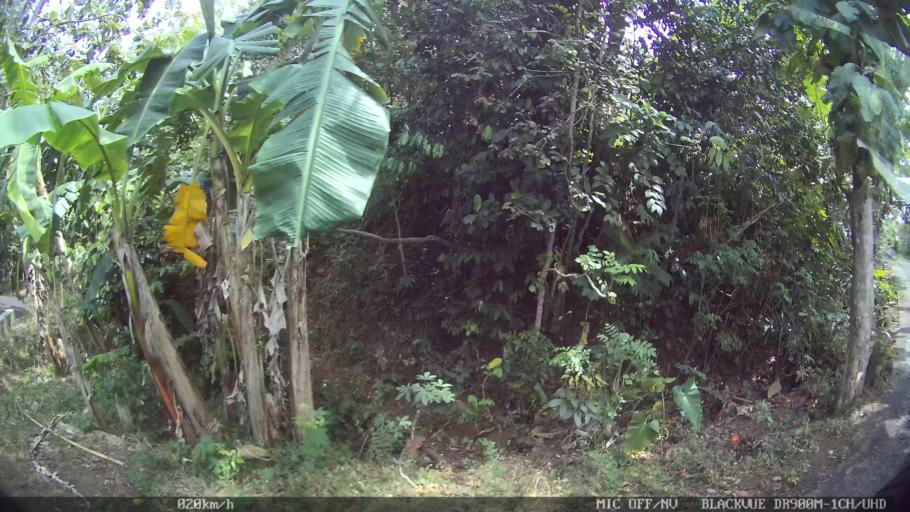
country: ID
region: Central Java
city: Candi Prambanan
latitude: -7.8189
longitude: 110.5247
